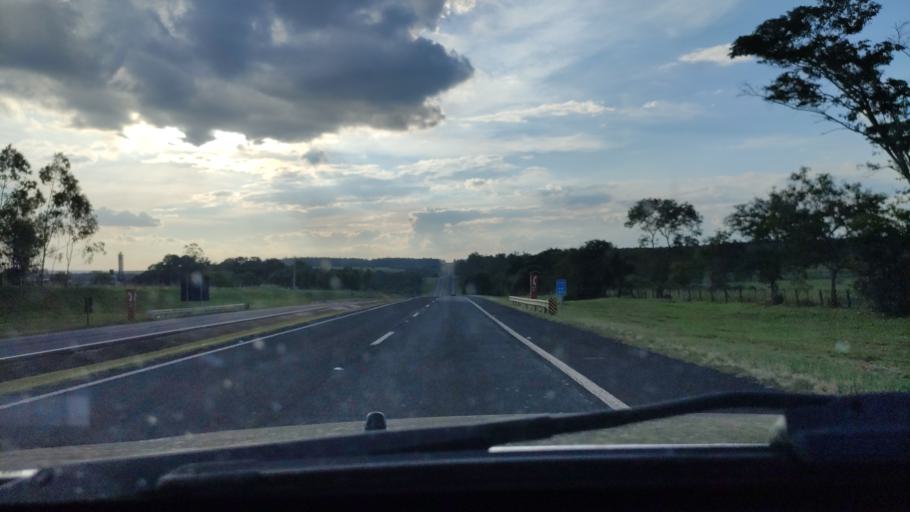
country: BR
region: Sao Paulo
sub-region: Rancharia
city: Rancharia
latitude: -22.4794
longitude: -50.9324
